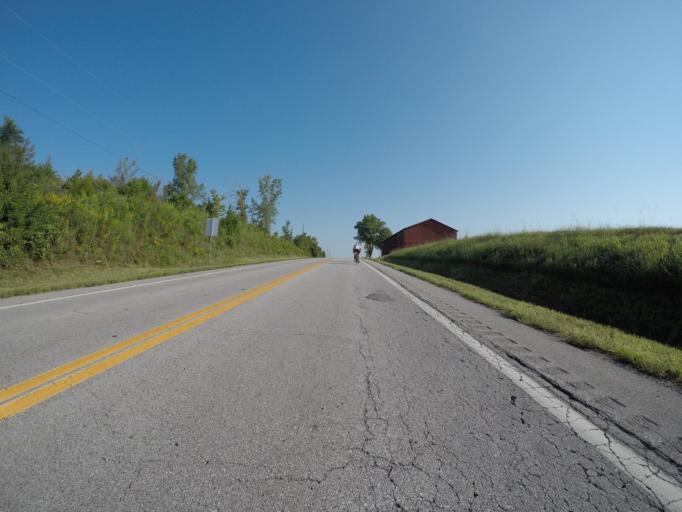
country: US
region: Missouri
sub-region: Platte County
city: Weston
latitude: 39.3958
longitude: -94.8633
